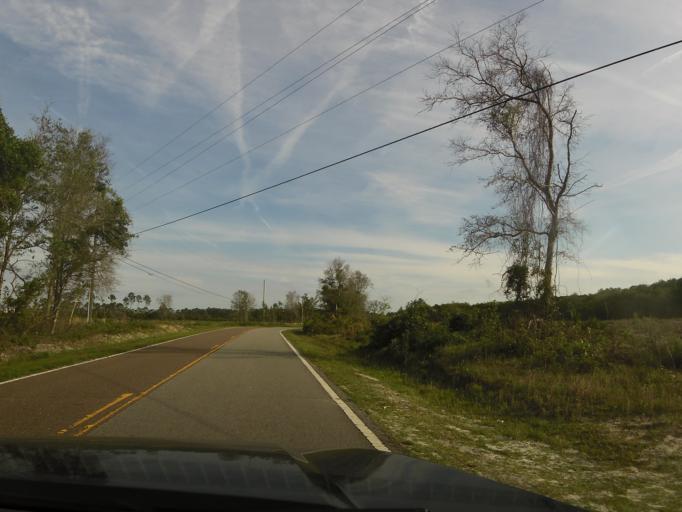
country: US
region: Florida
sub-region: Nassau County
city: Fernandina Beach
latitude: 30.4990
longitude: -81.4724
